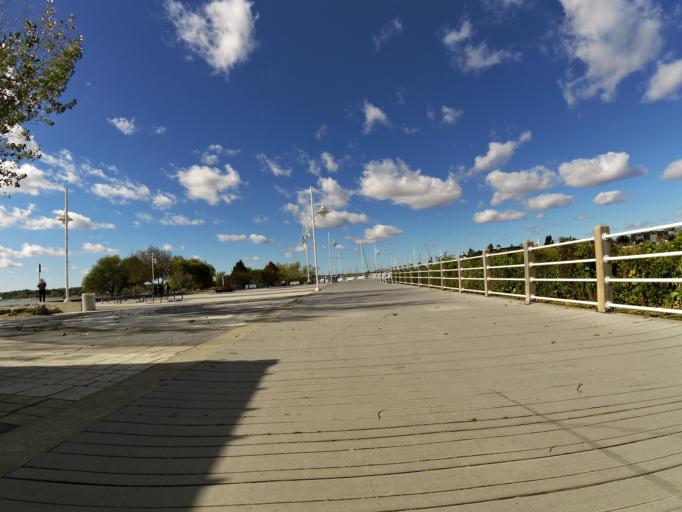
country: CA
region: Ontario
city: Ajax
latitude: 43.8126
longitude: -79.0799
